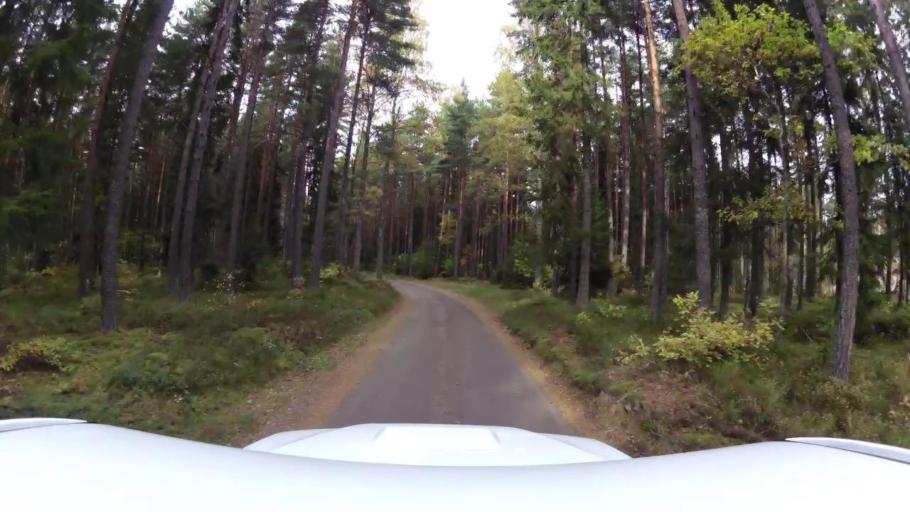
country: SE
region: OEstergoetland
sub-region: Linkopings Kommun
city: Ekangen
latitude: 58.5543
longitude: 15.6730
